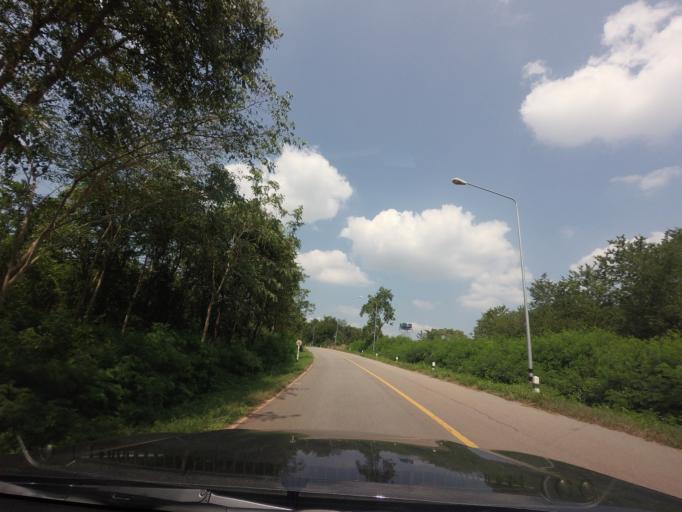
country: TH
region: Uttaradit
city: Ban Khok
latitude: 17.9212
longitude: 100.9975
